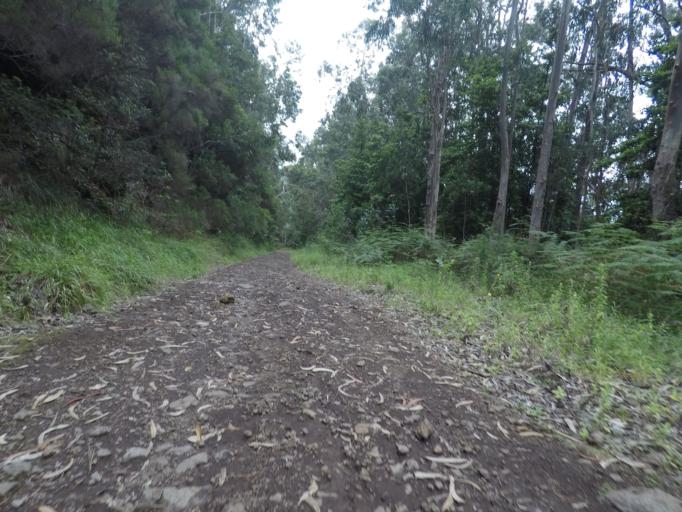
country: PT
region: Madeira
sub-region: Sao Vicente
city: Sao Vicente
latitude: 32.7758
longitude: -17.0508
